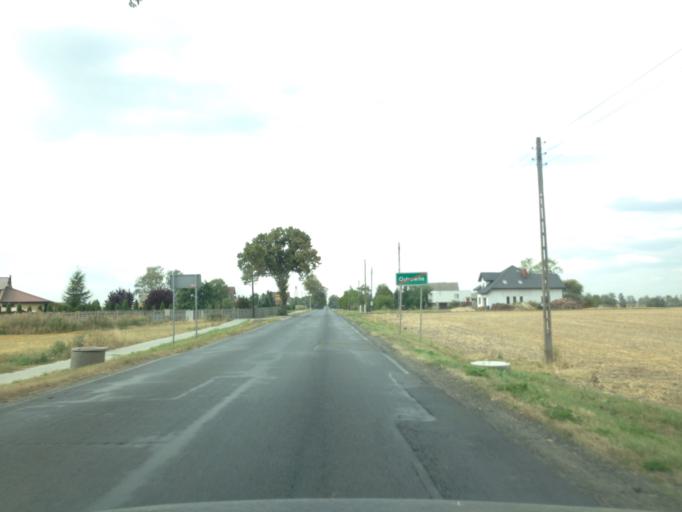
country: PL
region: Kujawsko-Pomorskie
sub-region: Powiat golubsko-dobrzynski
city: Kowalewo Pomorskie
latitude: 53.1476
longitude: 18.9673
